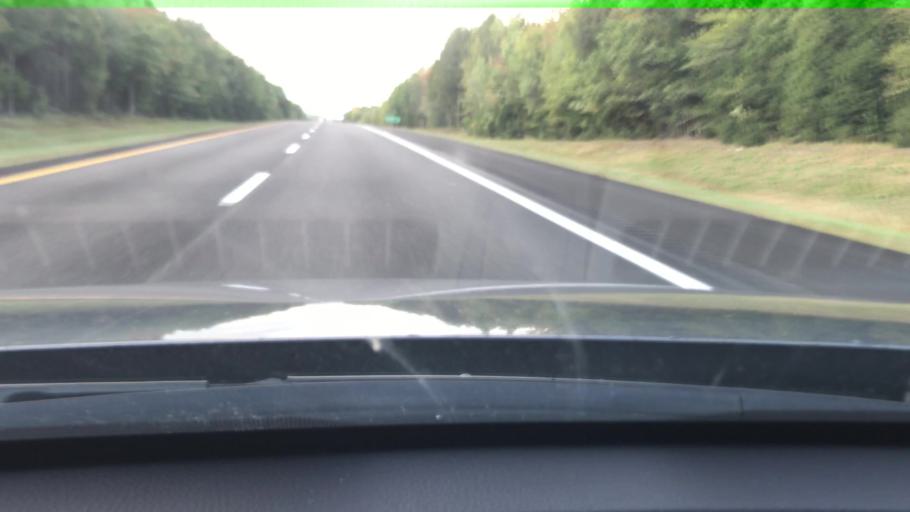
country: US
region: Maine
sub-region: Sagadahoc County
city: Richmond
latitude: 44.0908
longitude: -69.8752
